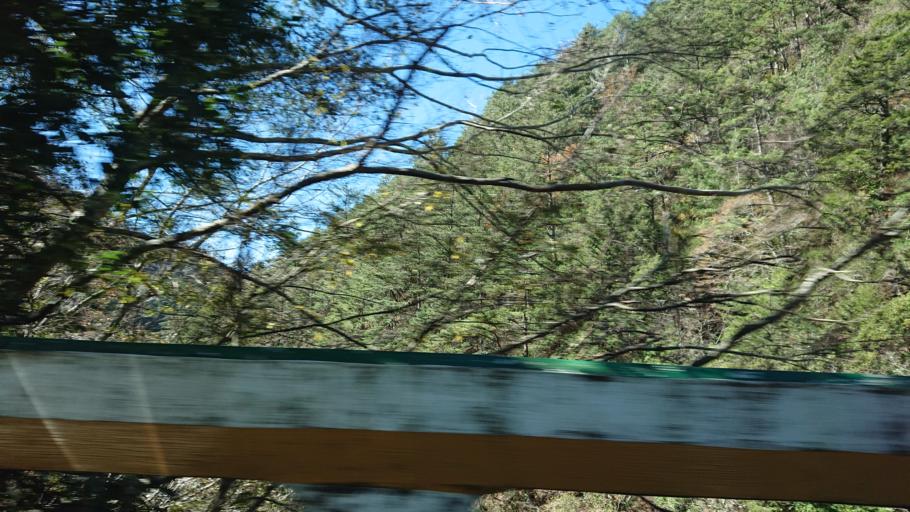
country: TW
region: Taiwan
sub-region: Hualien
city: Hualian
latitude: 24.3476
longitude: 121.3083
